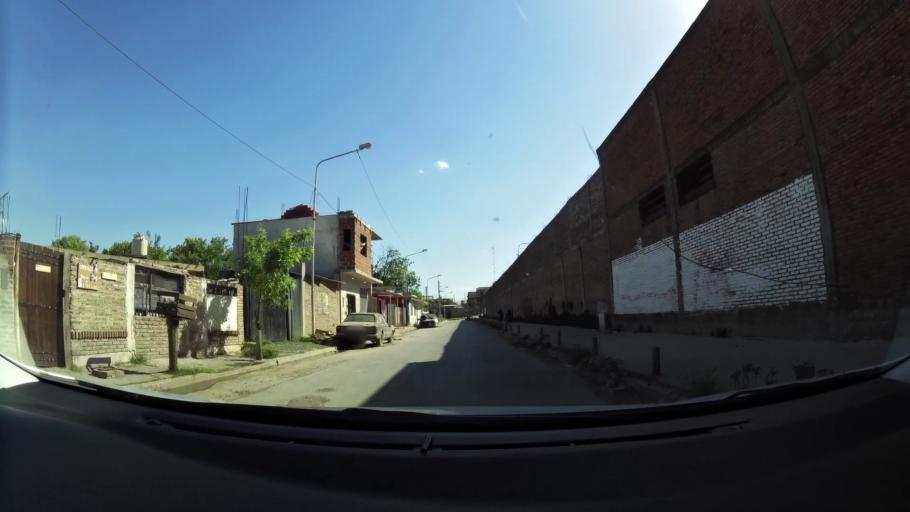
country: AR
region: Buenos Aires F.D.
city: Villa Lugano
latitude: -34.7063
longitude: -58.4806
